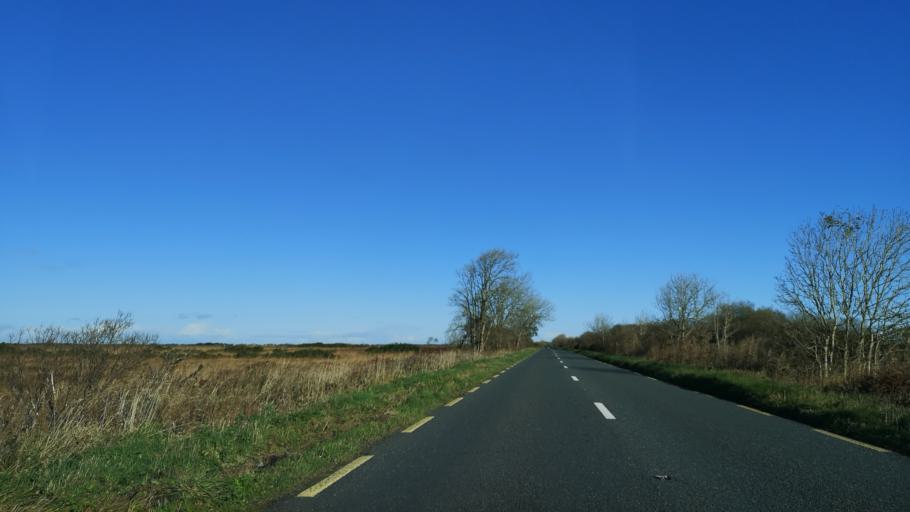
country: IE
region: Connaught
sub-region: County Galway
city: Claregalway
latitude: 53.3468
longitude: -9.0188
